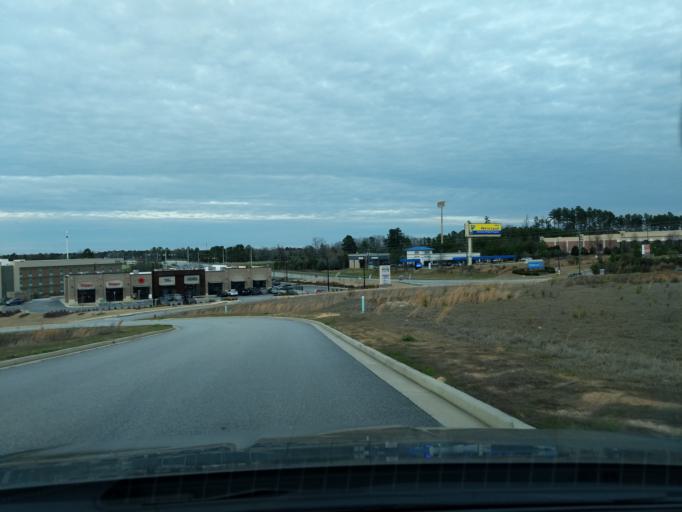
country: US
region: Georgia
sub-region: Columbia County
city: Grovetown
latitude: 33.4795
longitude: -82.1992
